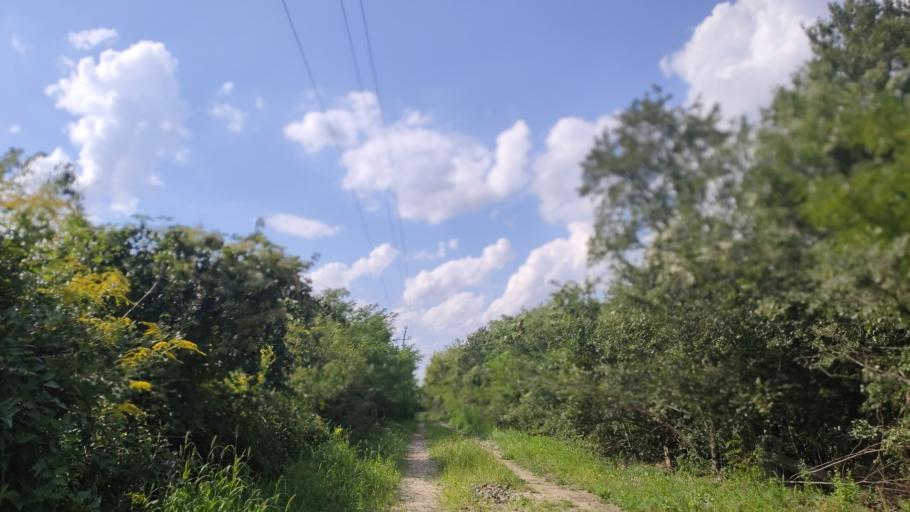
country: HU
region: Pest
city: Toeroekbalint
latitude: 47.4626
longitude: 18.8718
